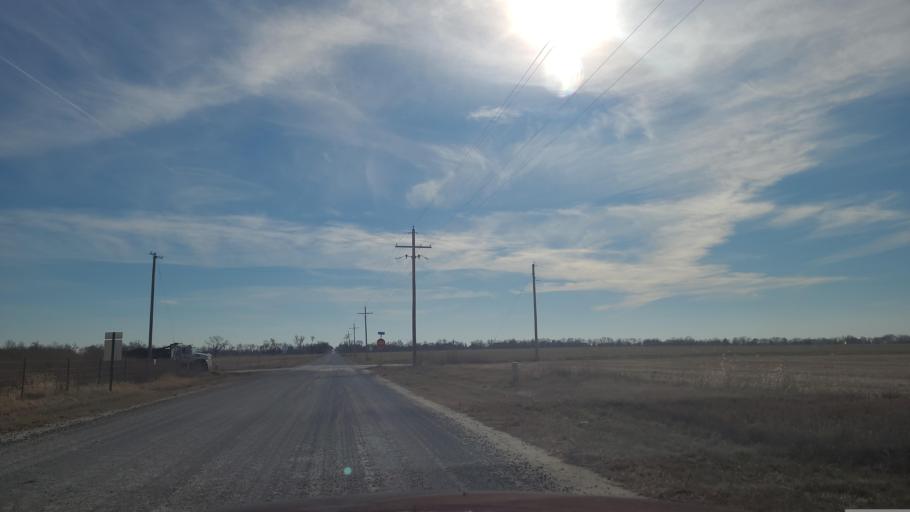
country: US
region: Kansas
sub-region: Douglas County
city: Eudora
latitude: 38.9140
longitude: -95.0748
